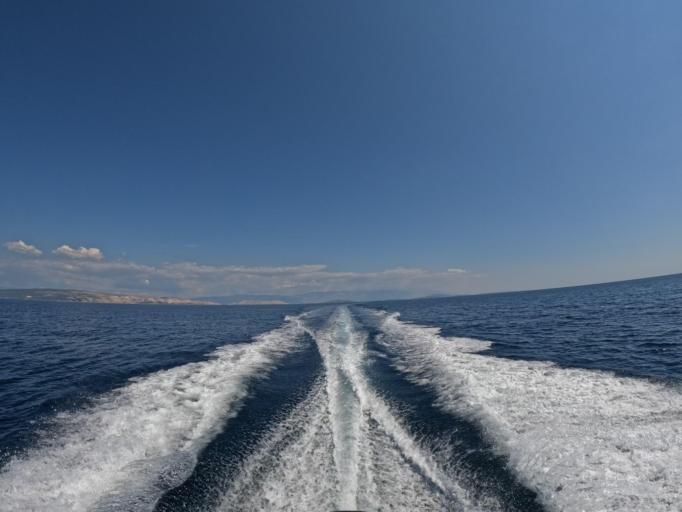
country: HR
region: Primorsko-Goranska
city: Cres
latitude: 44.9345
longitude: 14.5131
